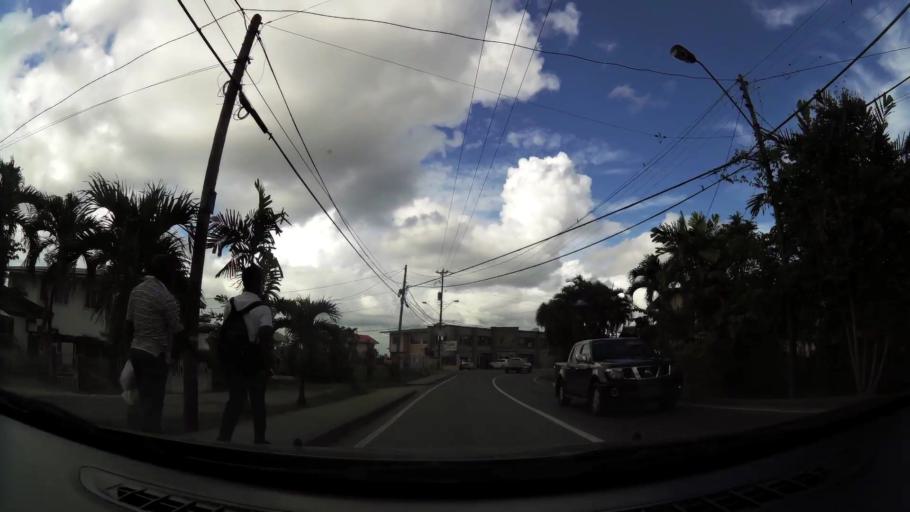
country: TT
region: City of San Fernando
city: Mon Repos
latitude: 10.2804
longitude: -61.4341
